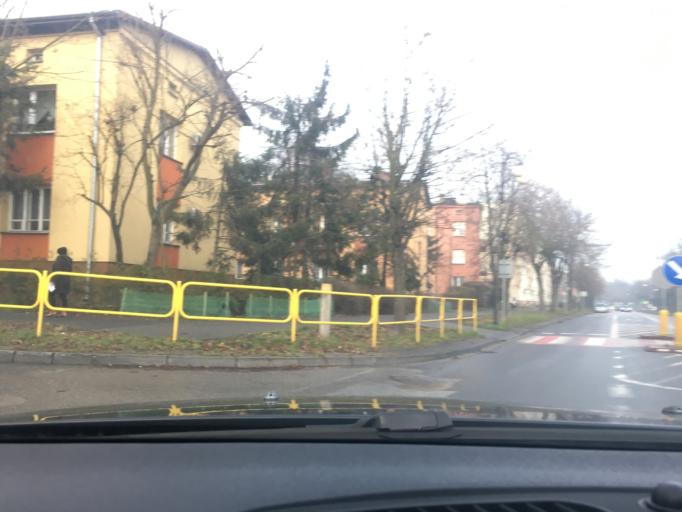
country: PL
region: Swietokrzyskie
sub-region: Powiat jedrzejowski
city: Jedrzejow
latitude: 50.6477
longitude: 20.2919
